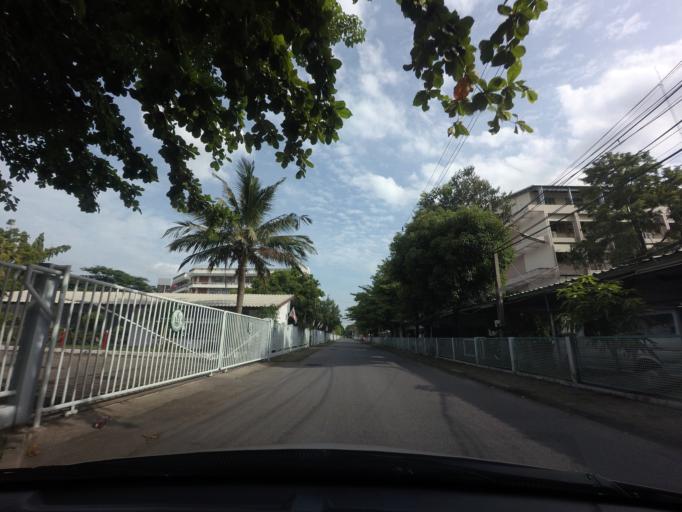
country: TH
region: Bangkok
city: Chatuchak
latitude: 13.8482
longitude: 100.5751
